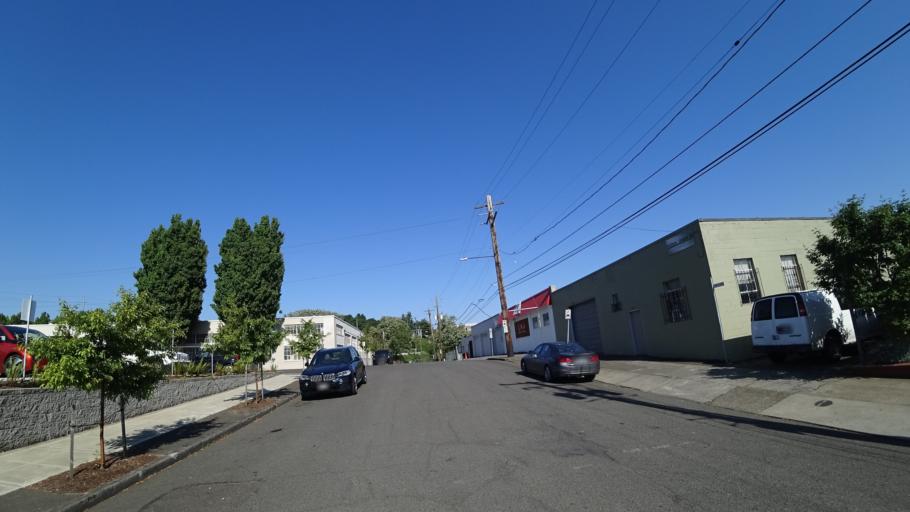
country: US
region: Oregon
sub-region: Multnomah County
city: Portland
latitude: 45.5396
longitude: -122.6742
